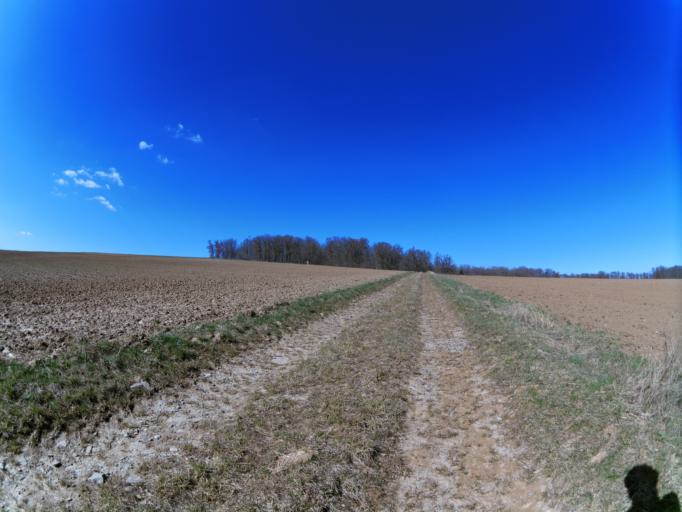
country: DE
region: Bavaria
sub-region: Regierungsbezirk Unterfranken
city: Hettstadt
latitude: 49.8019
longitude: 9.7897
